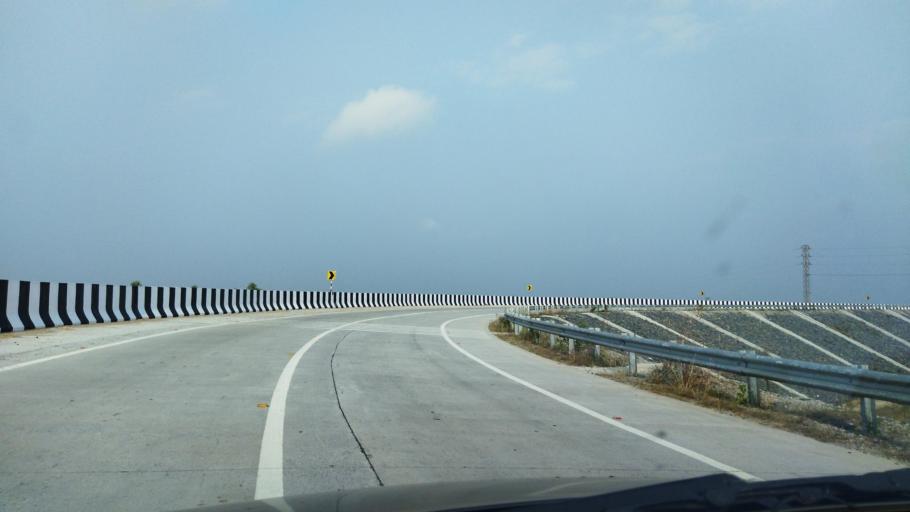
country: IN
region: Telangana
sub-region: Nalgonda
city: Nalgonda
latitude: 17.1668
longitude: 79.3956
